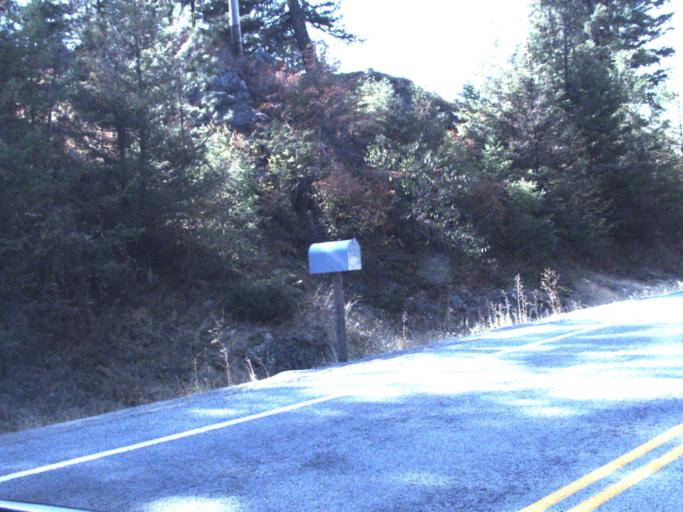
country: US
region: Washington
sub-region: Pend Oreille County
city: Newport
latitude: 48.1365
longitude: -117.2857
